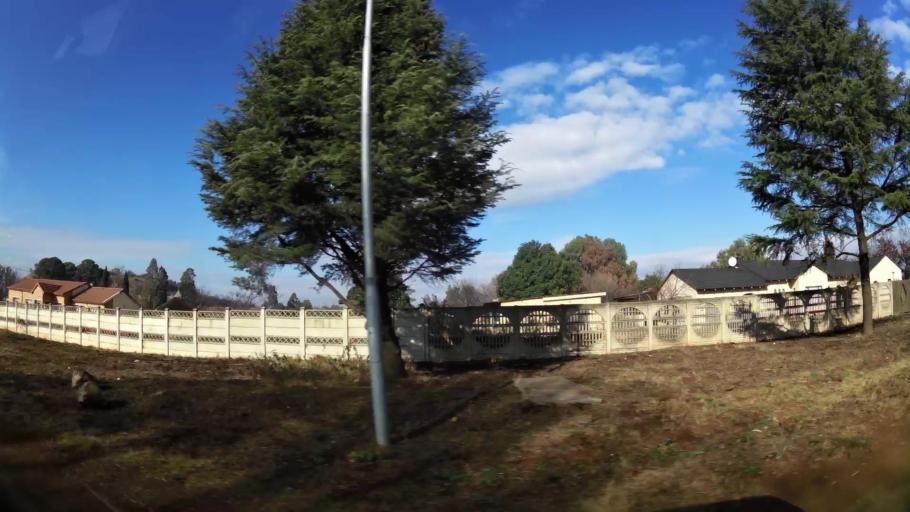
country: ZA
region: Gauteng
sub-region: Sedibeng District Municipality
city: Meyerton
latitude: -26.5040
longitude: 28.0678
